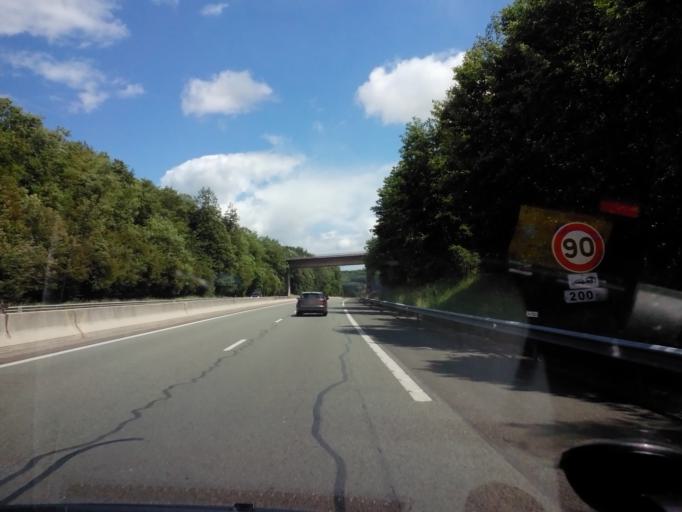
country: FR
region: Champagne-Ardenne
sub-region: Departement de la Haute-Marne
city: Avrecourt
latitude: 47.9649
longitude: 5.4741
